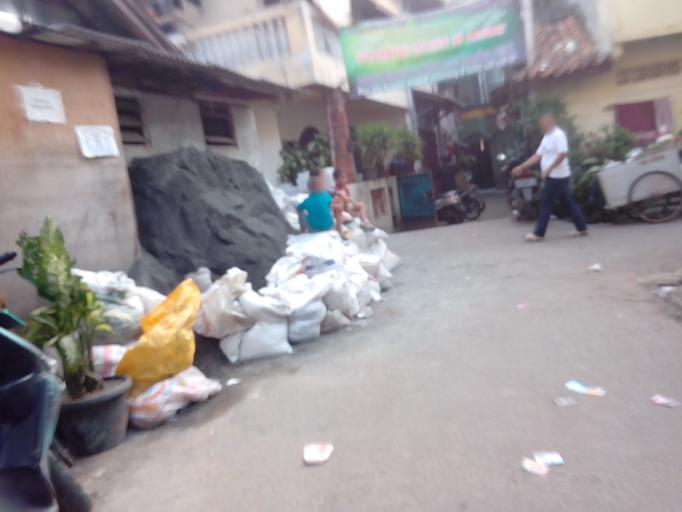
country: ID
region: Jakarta Raya
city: Jakarta
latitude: -6.1938
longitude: 106.8115
